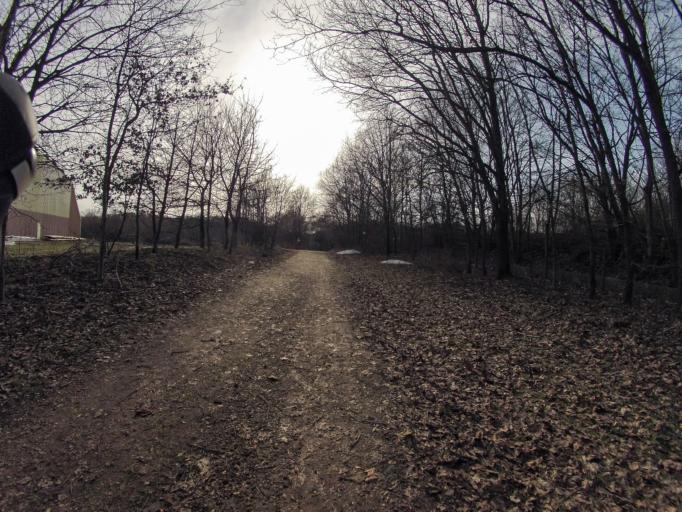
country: DE
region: North Rhine-Westphalia
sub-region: Regierungsbezirk Munster
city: Rheine
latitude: 52.3109
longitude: 7.4206
